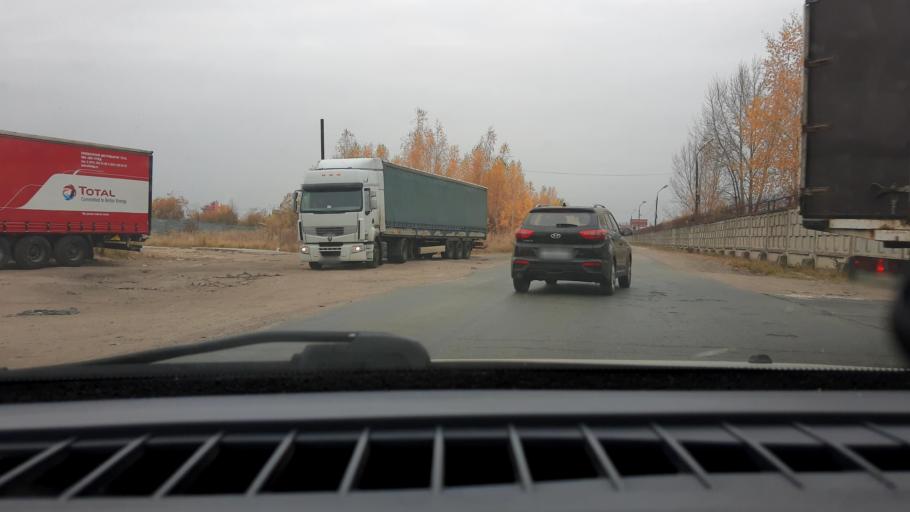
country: RU
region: Nizjnij Novgorod
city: Gorbatovka
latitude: 56.3323
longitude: 43.8064
